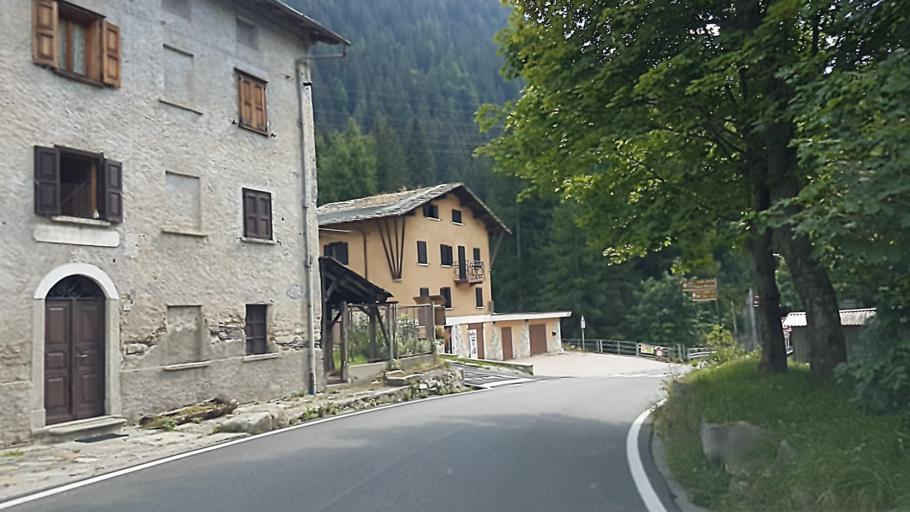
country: IT
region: Lombardy
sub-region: Provincia di Sondrio
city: Campodolcino
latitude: 46.4269
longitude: 9.3447
